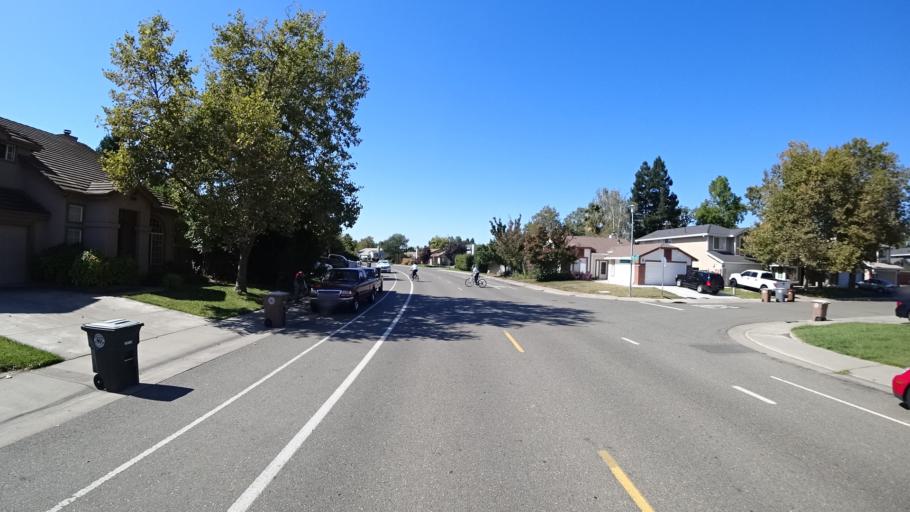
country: US
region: California
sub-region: Sacramento County
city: Laguna
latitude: 38.4281
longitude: -121.4251
